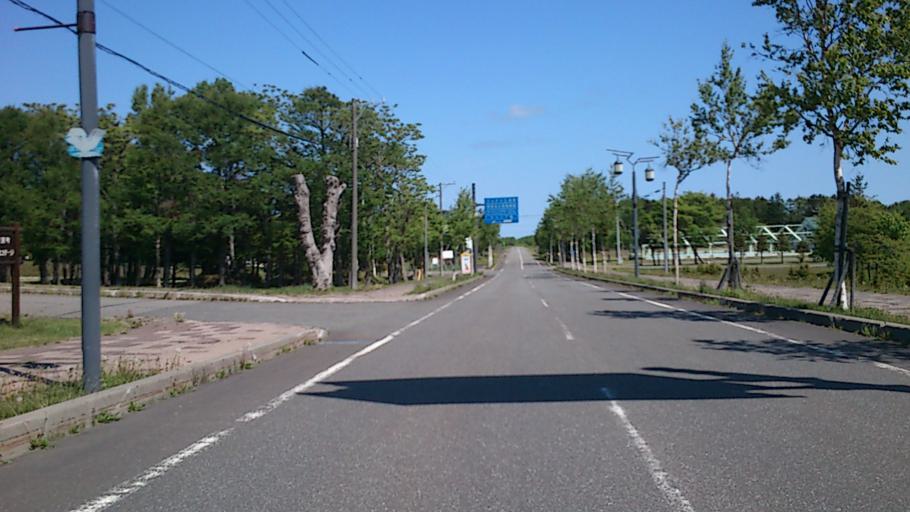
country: JP
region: Hokkaido
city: Makubetsu
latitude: 45.1236
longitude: 142.3505
